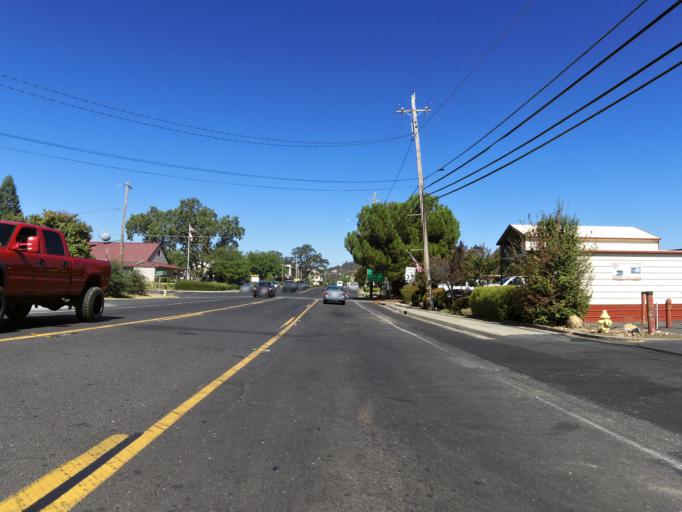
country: US
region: California
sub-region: Calaveras County
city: Angels Camp
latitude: 38.0808
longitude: -120.5565
